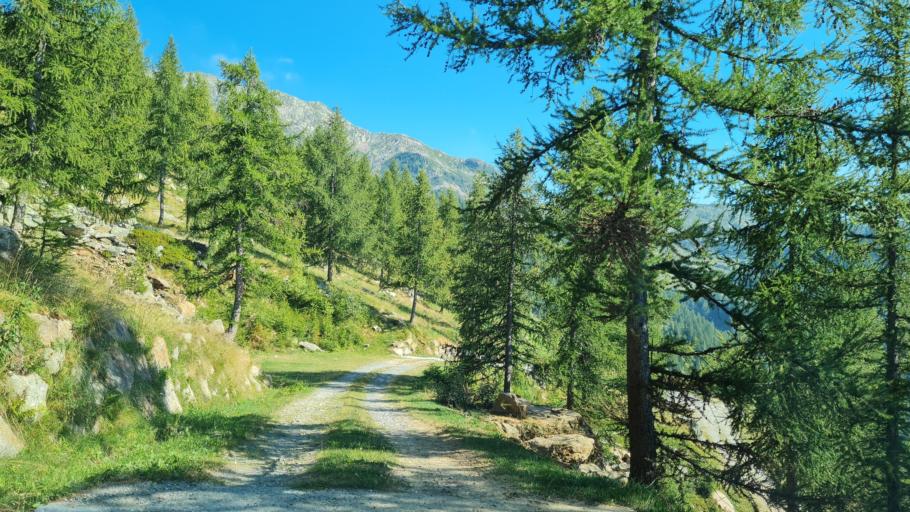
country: IT
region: Aosta Valley
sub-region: Valle d'Aosta
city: Fontainemore
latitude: 45.6203
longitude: 7.8766
